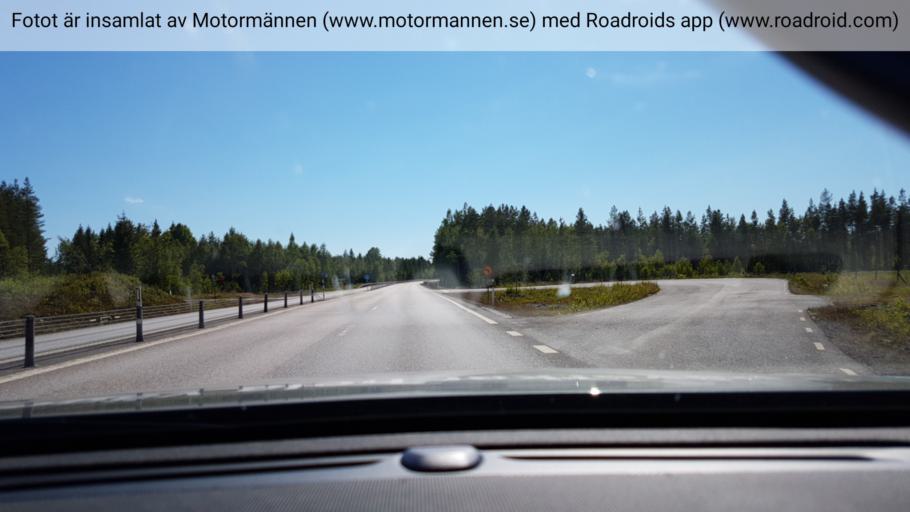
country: SE
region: Vaesterbotten
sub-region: Umea Kommun
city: Saevar
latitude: 63.9701
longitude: 20.7093
